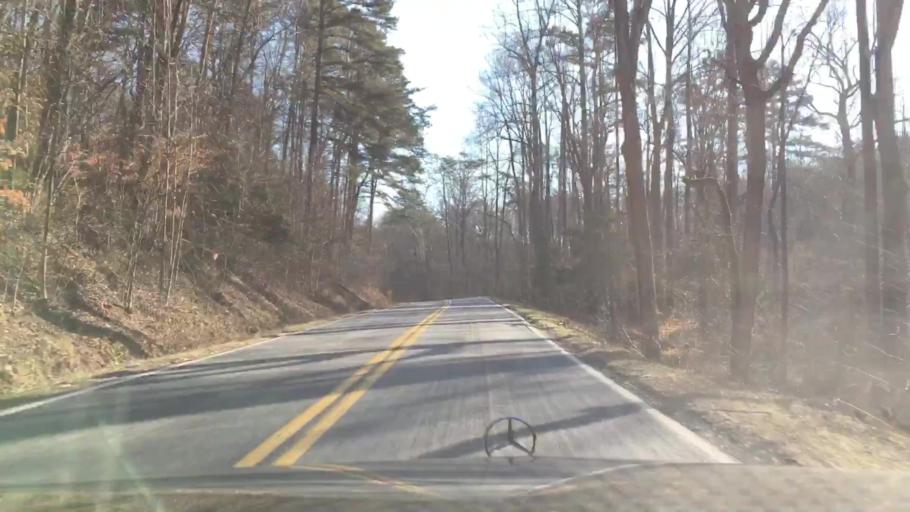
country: US
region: Virginia
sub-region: Campbell County
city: Altavista
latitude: 37.1435
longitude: -79.3278
